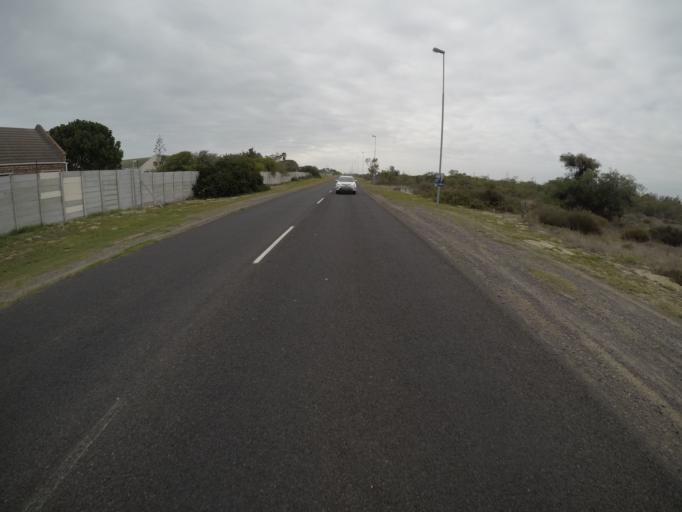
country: ZA
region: Western Cape
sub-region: City of Cape Town
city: Atlantis
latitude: -33.7070
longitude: 18.4470
